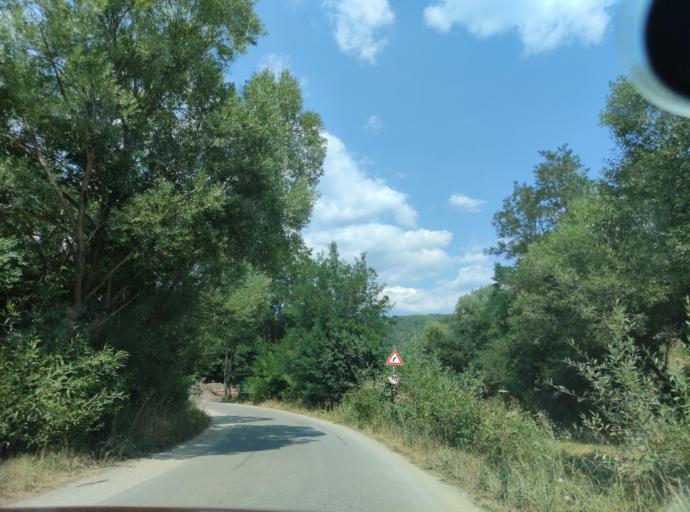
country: BG
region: Blagoevgrad
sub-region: Obshtina Belitsa
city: Belitsa
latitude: 41.9805
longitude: 23.5531
